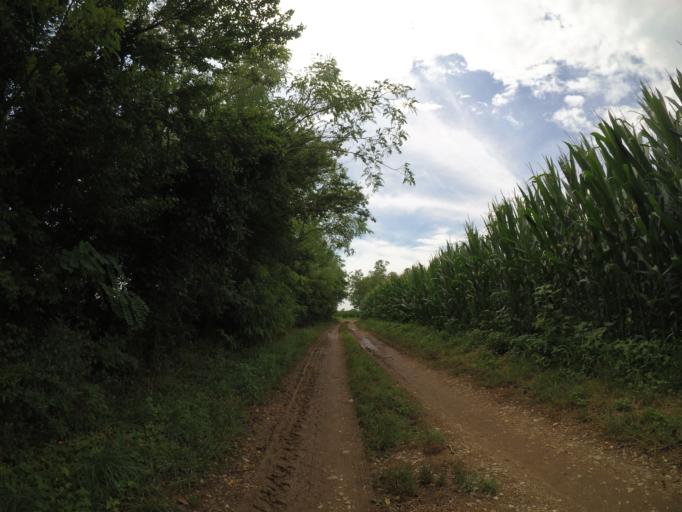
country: IT
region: Friuli Venezia Giulia
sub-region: Provincia di Udine
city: Bertiolo
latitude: 45.9672
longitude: 13.0632
